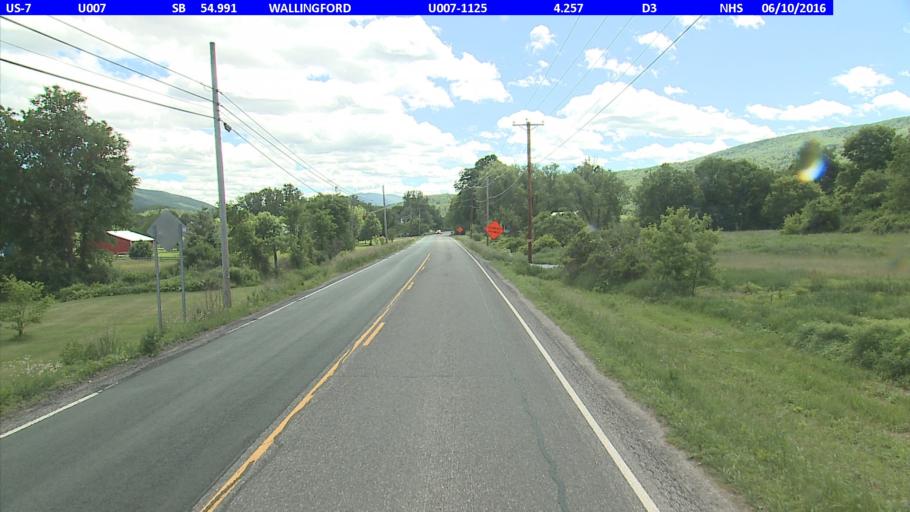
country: US
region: Vermont
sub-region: Rutland County
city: West Rutland
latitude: 43.4565
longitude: -72.9840
